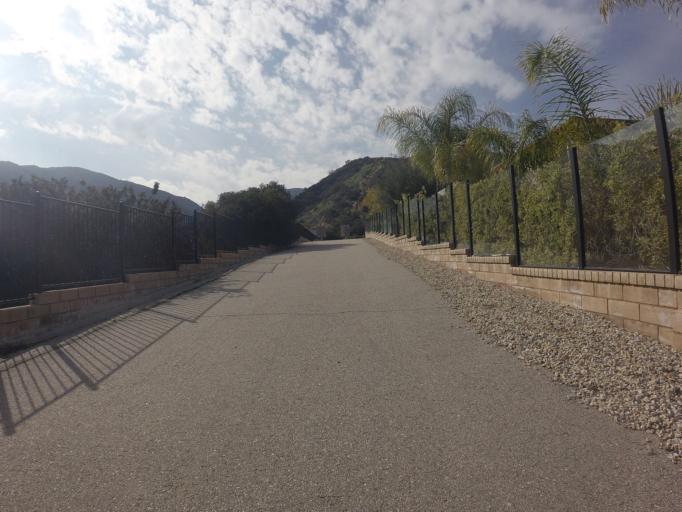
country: US
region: California
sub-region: Riverside County
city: Corona
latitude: 33.8368
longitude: -117.6010
